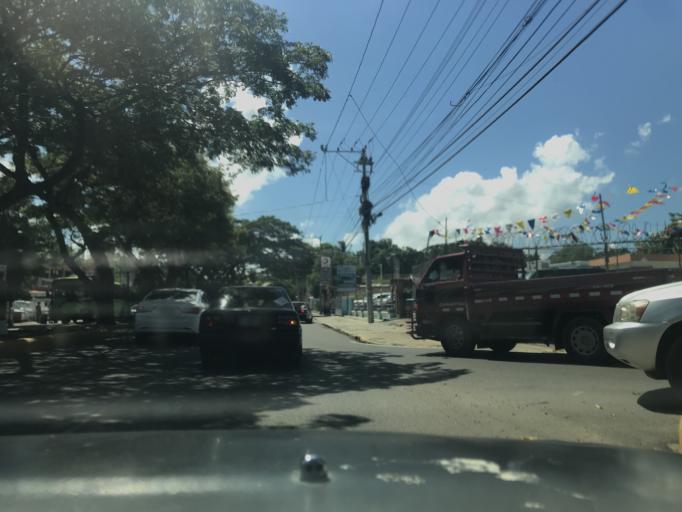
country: DO
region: Santiago
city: Santiago de los Caballeros
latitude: 19.4397
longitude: -70.7223
